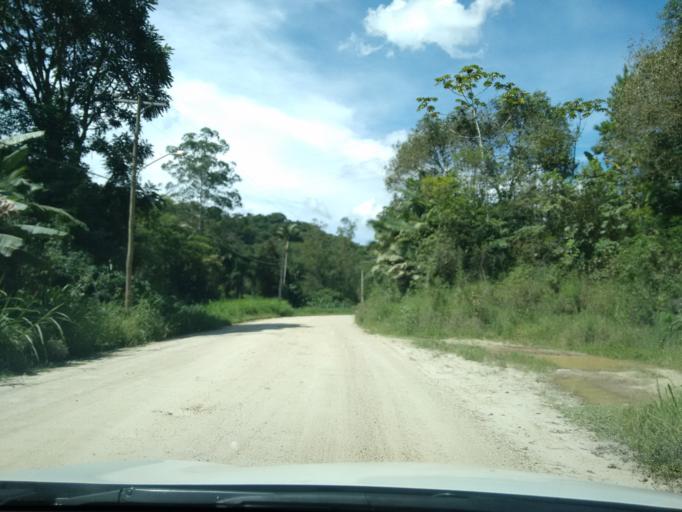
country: BR
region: Santa Catarina
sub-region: Pomerode
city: Pomerode
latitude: -26.6946
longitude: -49.1145
